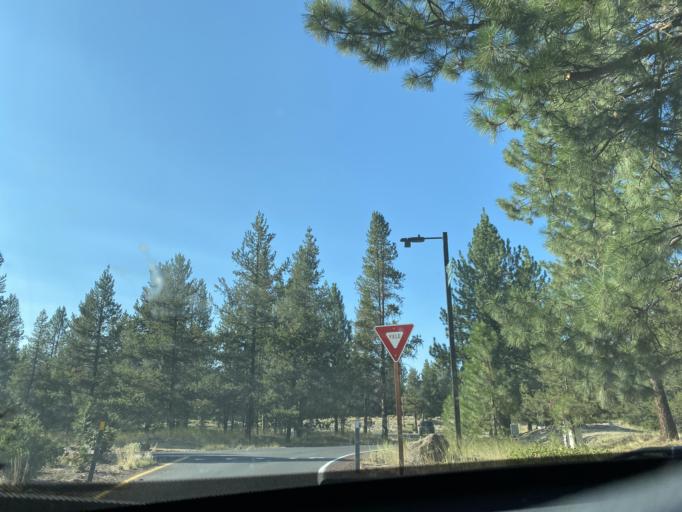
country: US
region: Oregon
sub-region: Deschutes County
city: Sunriver
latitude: 43.8822
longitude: -121.4387
